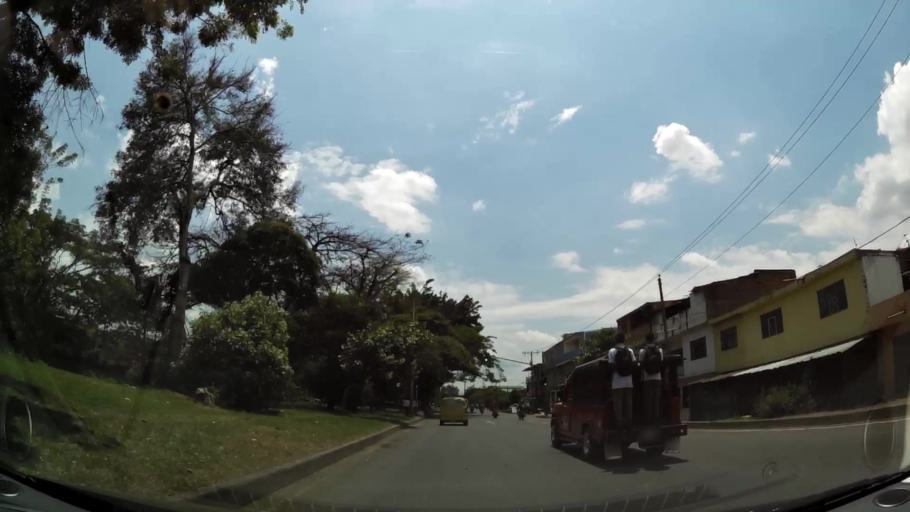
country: CO
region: Valle del Cauca
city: Cali
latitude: 3.4491
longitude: -76.4836
